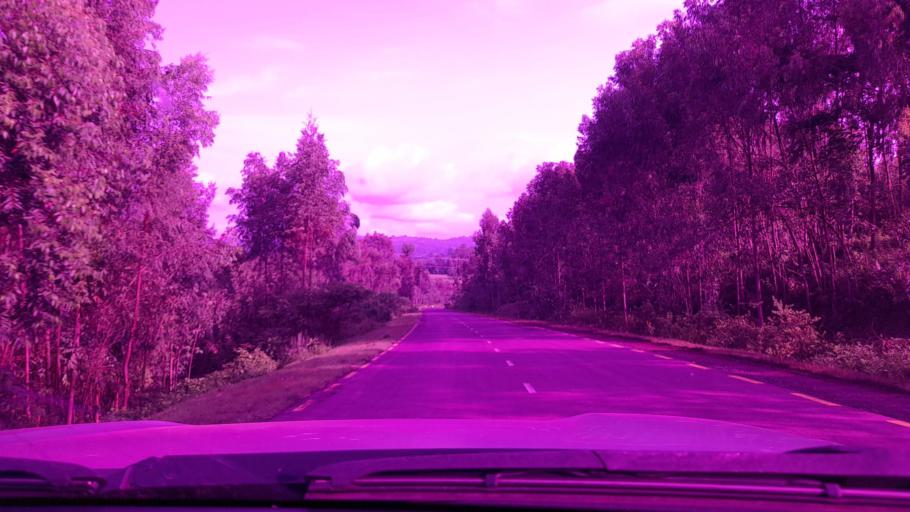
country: ET
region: Oromiya
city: Bedele
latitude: 8.2022
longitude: 36.4414
